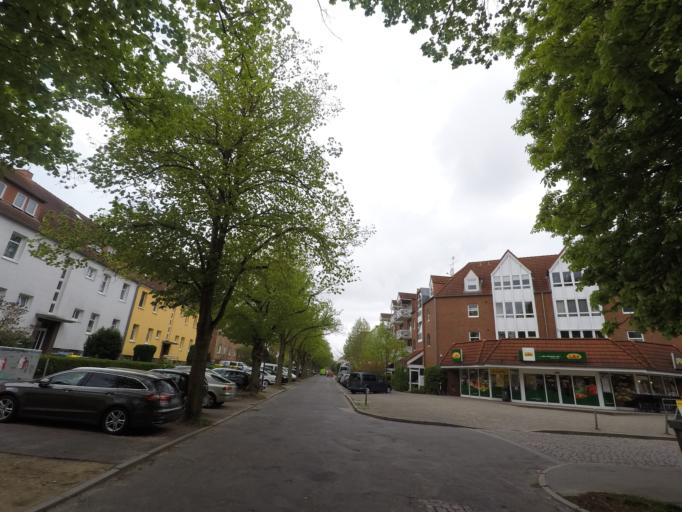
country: DE
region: Mecklenburg-Vorpommern
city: Rostock
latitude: 54.0794
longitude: 12.1075
